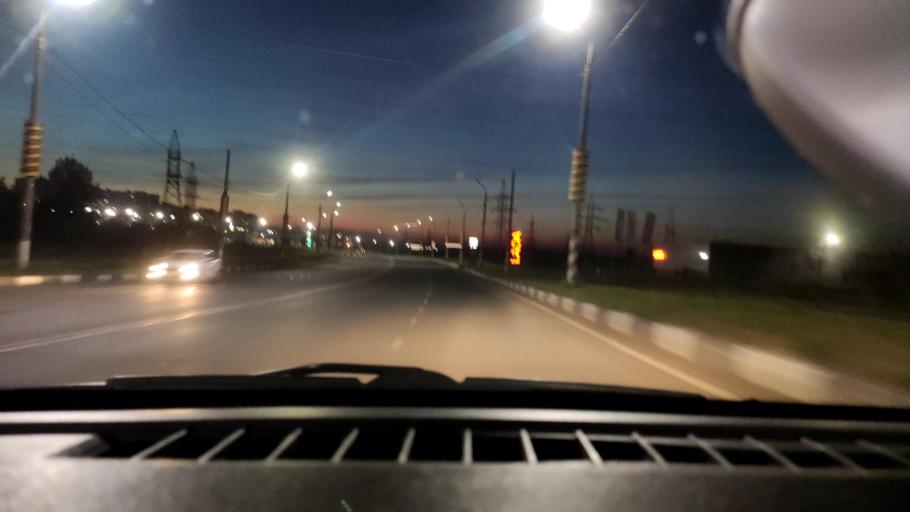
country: RU
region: Samara
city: Novokuybyshevsk
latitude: 53.0837
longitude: 49.9991
